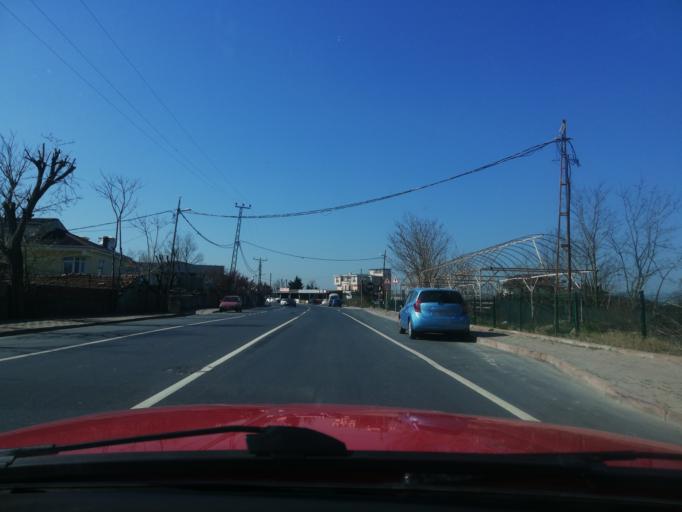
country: TR
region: Istanbul
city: Umraniye
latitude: 41.0723
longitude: 29.1595
